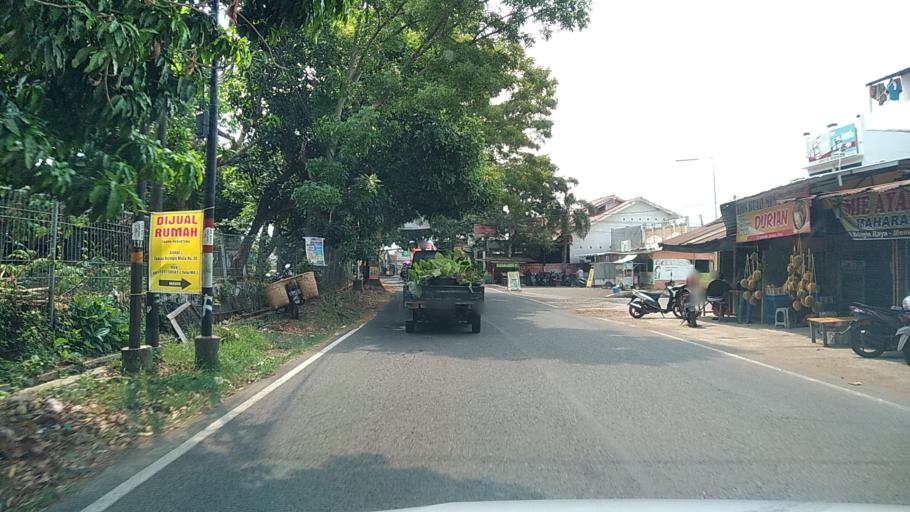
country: ID
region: Central Java
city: Semarang
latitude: -6.9968
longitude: 110.3362
